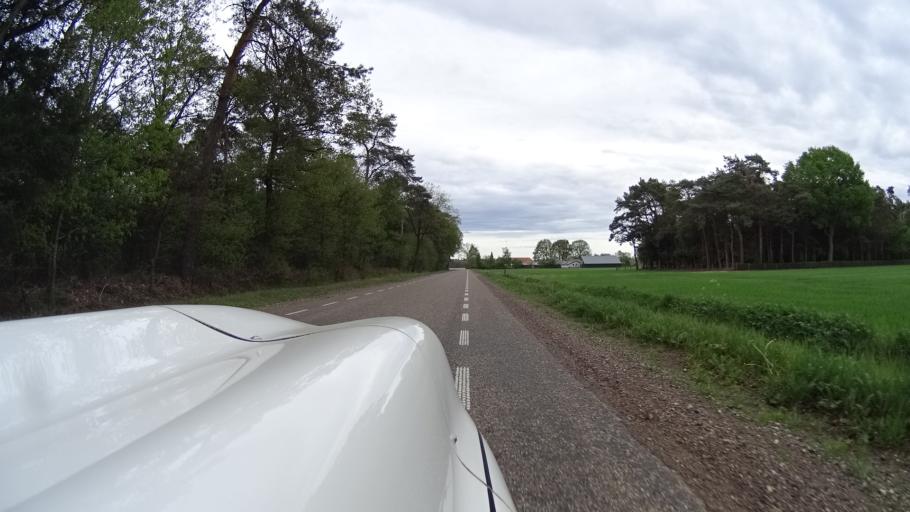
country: NL
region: North Brabant
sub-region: Gemeente Boxmeer
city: Overloon
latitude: 51.5464
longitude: 5.9381
